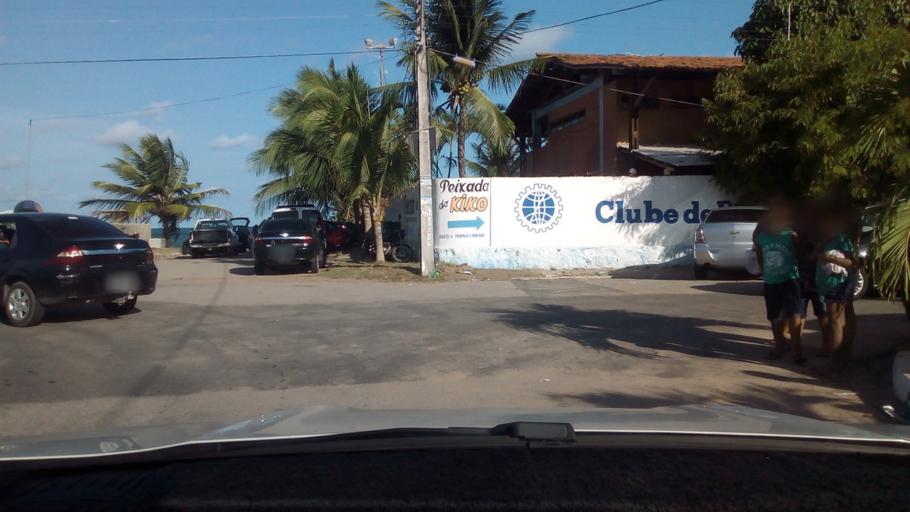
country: BR
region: Paraiba
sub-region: Joao Pessoa
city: Joao Pessoa
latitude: -7.1596
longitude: -34.7952
